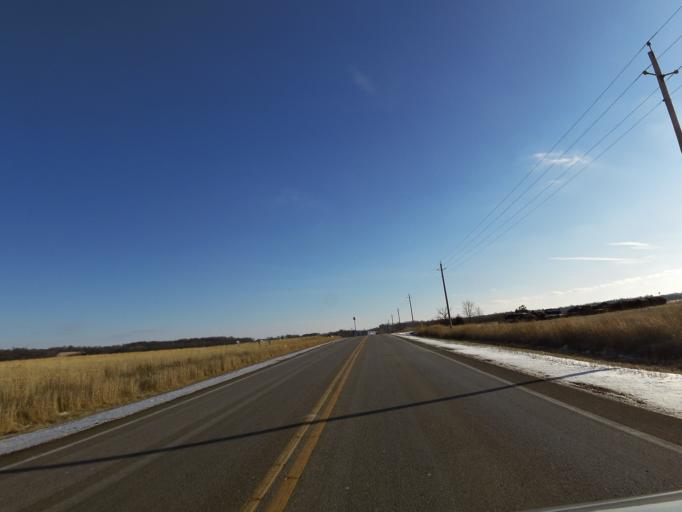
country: US
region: Minnesota
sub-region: Scott County
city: Prior Lake
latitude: 44.7678
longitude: -93.4494
